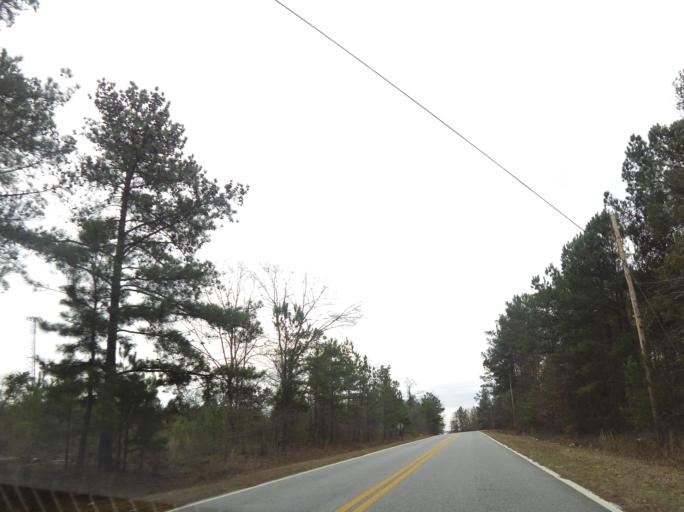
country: US
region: Georgia
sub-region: Bibb County
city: West Point
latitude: 32.8199
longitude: -83.7361
